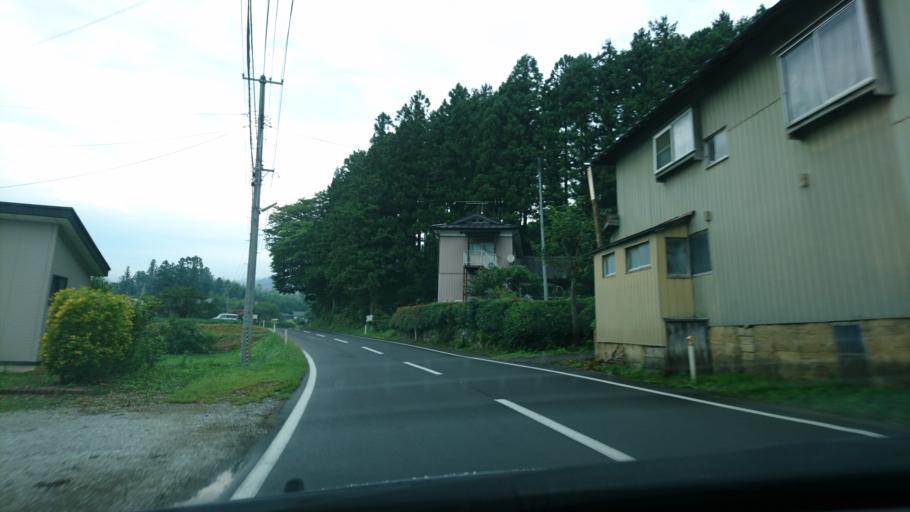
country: JP
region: Iwate
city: Ichinoseki
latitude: 38.9474
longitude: 141.2532
